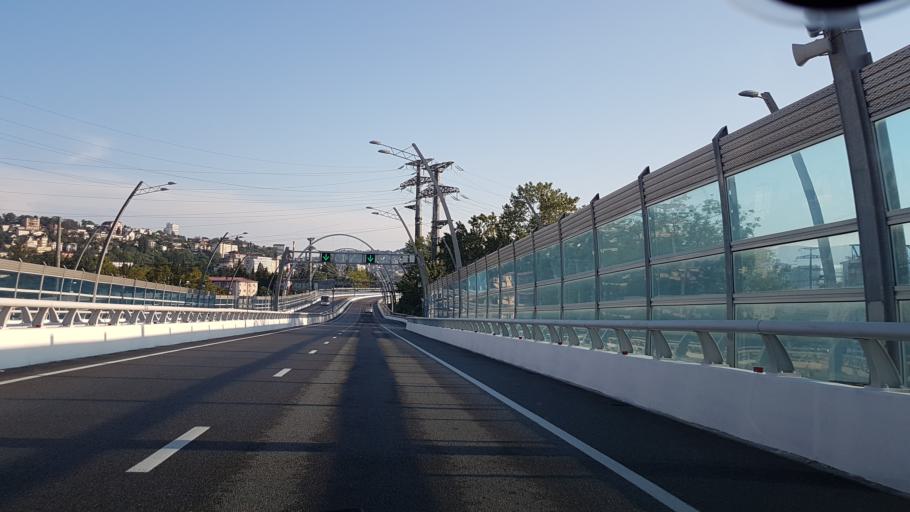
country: RU
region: Krasnodarskiy
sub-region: Sochi City
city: Sochi
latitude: 43.5982
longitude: 39.7313
